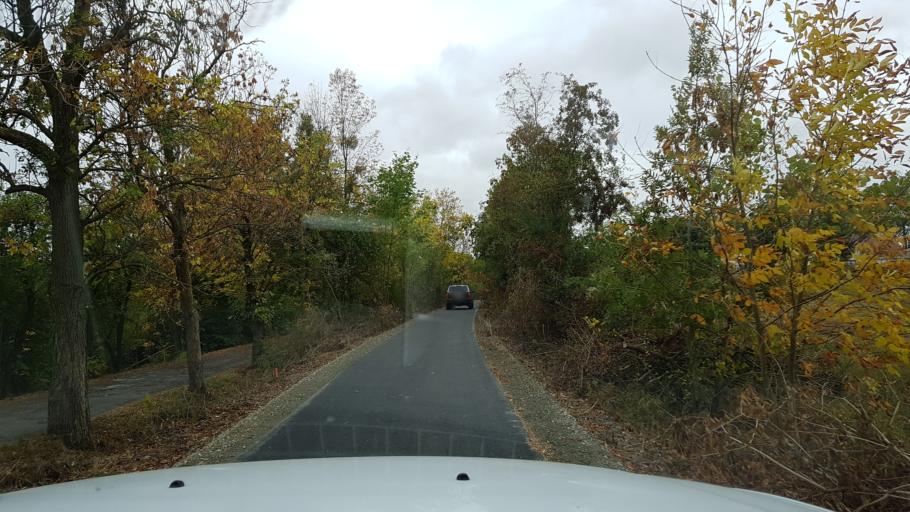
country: PL
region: West Pomeranian Voivodeship
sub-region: Powiat gryfinski
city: Moryn
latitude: 52.8733
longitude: 14.4002
